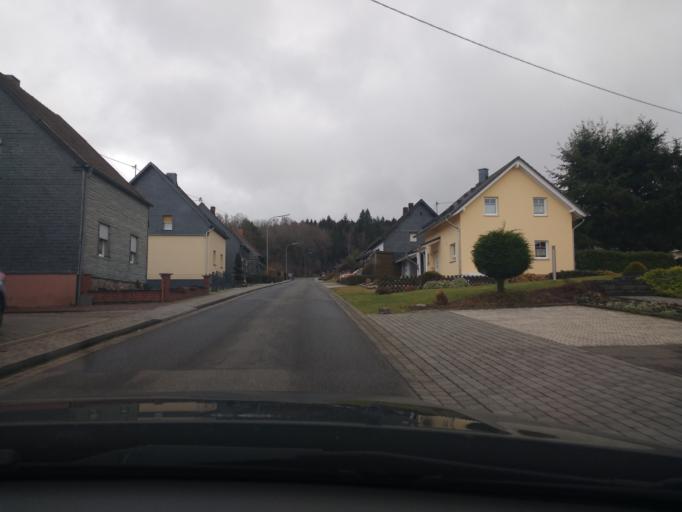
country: DE
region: Rheinland-Pfalz
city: Waldweiler
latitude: 49.6101
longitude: 6.8046
